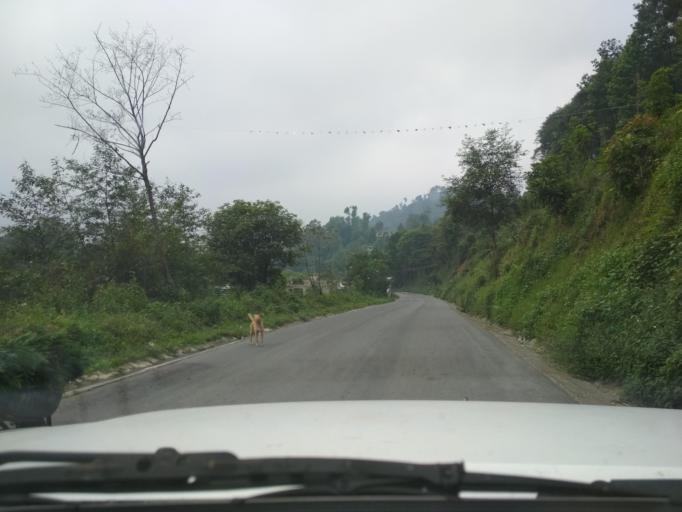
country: MX
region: Veracruz
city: La Perla
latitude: 18.9351
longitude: -97.1427
